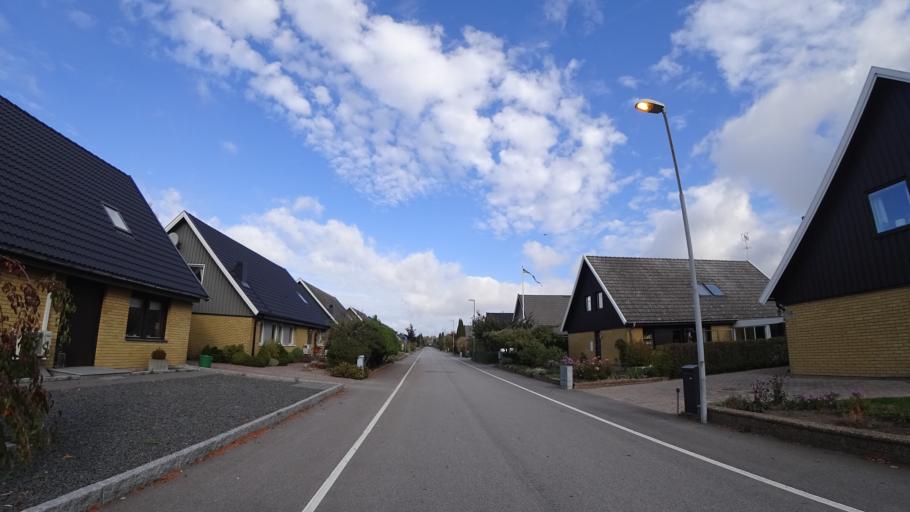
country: SE
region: Skane
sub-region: Staffanstorps Kommun
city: Staffanstorp
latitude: 55.6327
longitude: 13.1871
